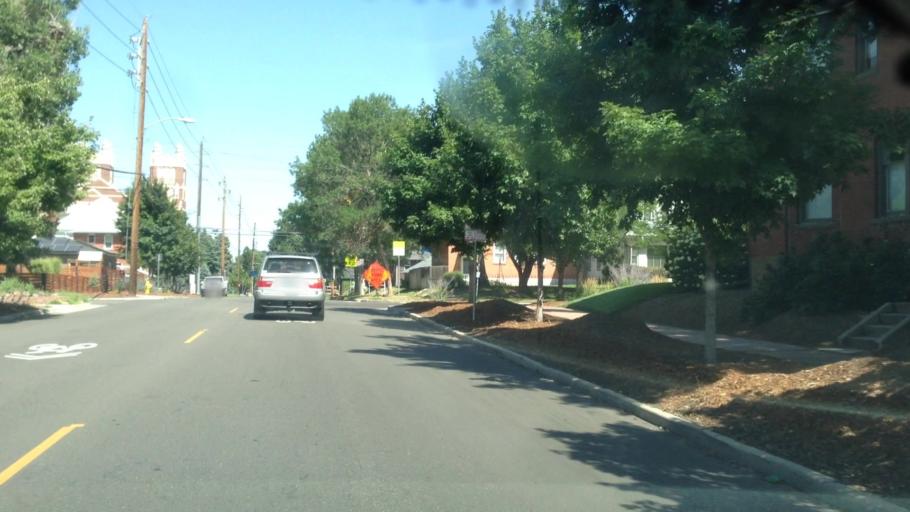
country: US
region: Colorado
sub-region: Denver County
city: Denver
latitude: 39.7507
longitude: -104.9628
